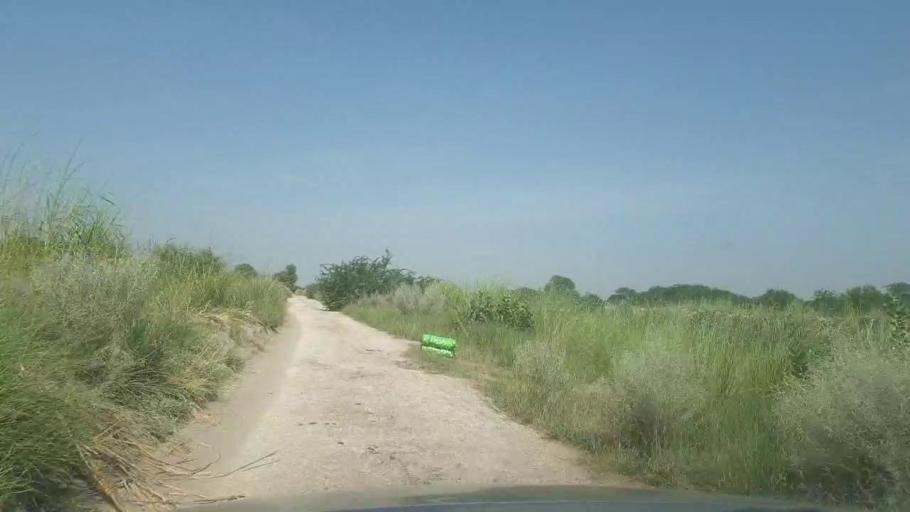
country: PK
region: Sindh
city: Khairpur
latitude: 27.3990
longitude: 69.0588
